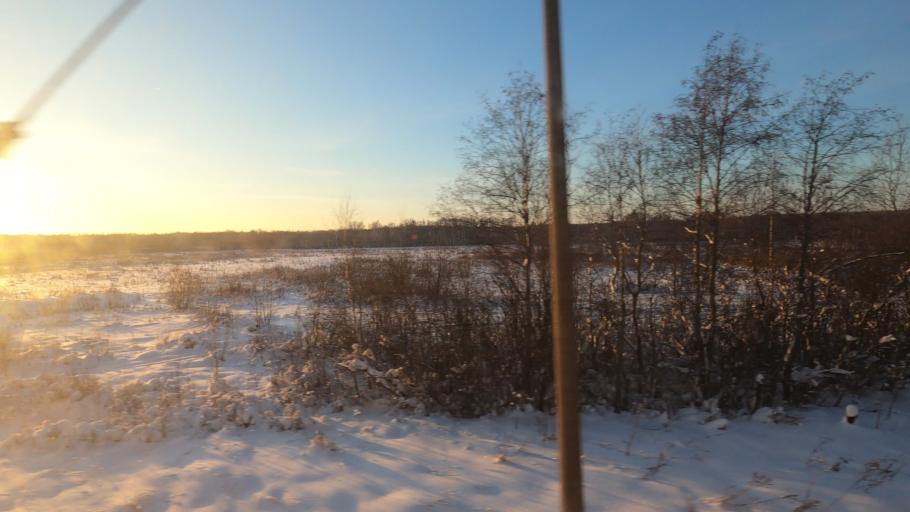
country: RU
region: Moskovskaya
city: Orud'yevo
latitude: 56.4168
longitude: 37.4972
